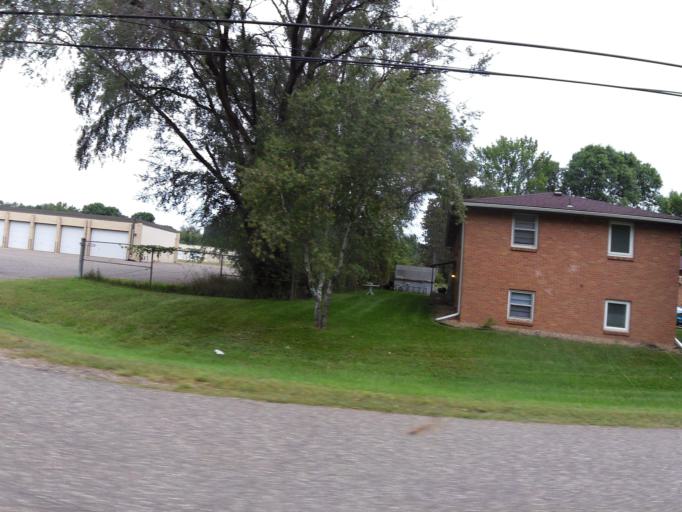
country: US
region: Minnesota
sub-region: Dakota County
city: Hastings
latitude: 44.7205
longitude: -92.8631
